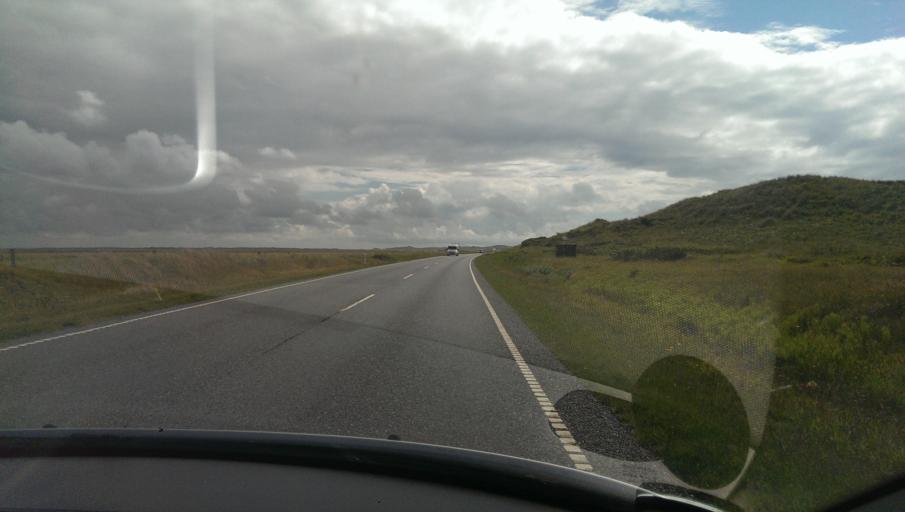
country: DK
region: Central Jutland
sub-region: Ringkobing-Skjern Kommune
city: Ringkobing
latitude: 56.2003
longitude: 8.1311
